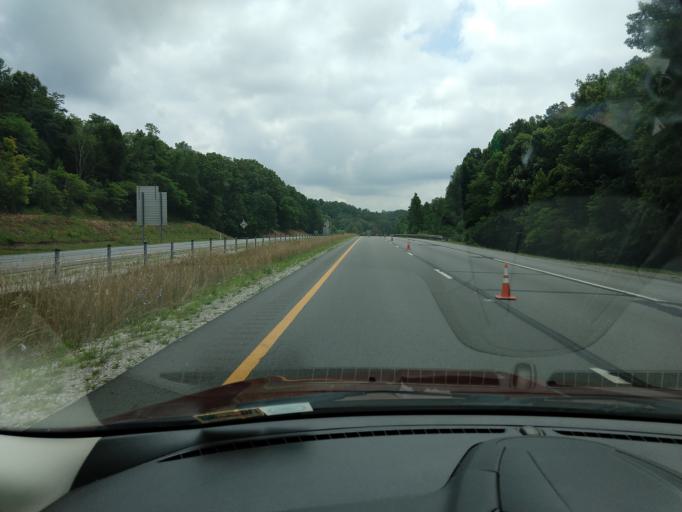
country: US
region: West Virginia
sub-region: Jackson County
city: Ripley
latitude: 38.8069
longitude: -81.7288
